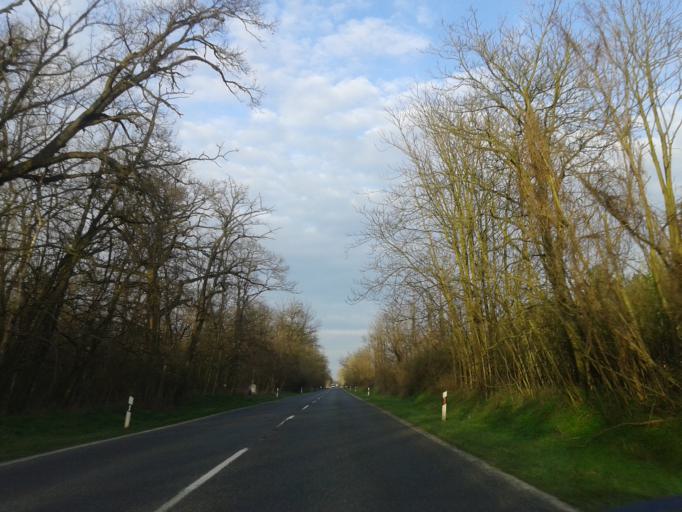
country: HU
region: Komarom-Esztergom
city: Acs
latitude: 47.7276
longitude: 18.0513
